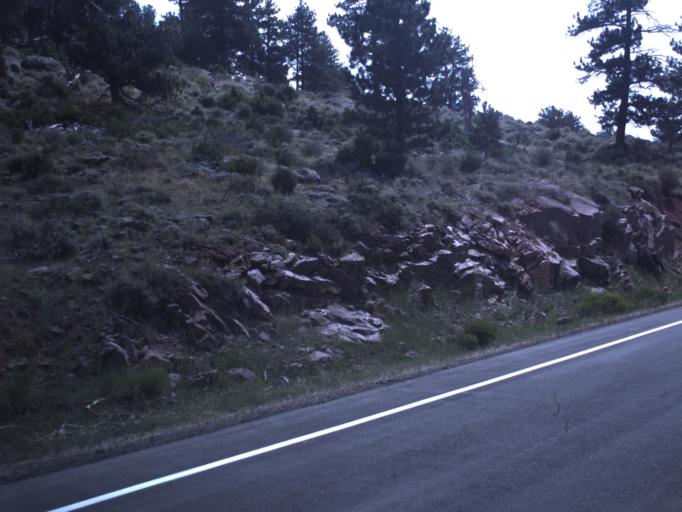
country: US
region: Utah
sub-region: Daggett County
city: Manila
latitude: 40.8858
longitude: -109.7018
